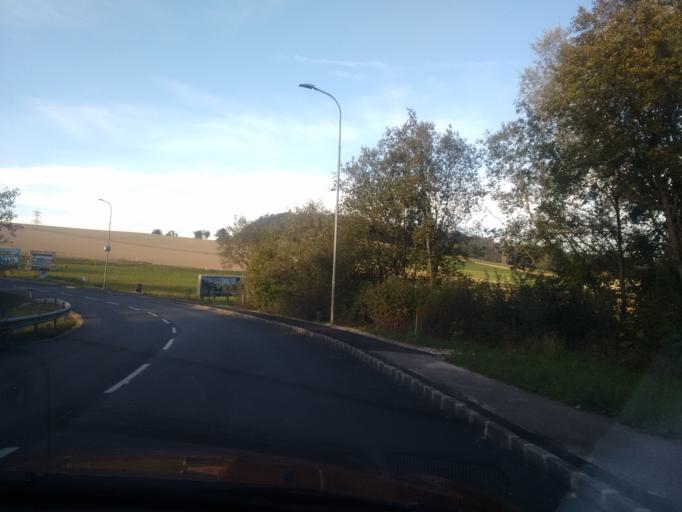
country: AT
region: Upper Austria
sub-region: Politischer Bezirk Vocklabruck
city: Niederthalheim
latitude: 48.1467
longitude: 13.7351
